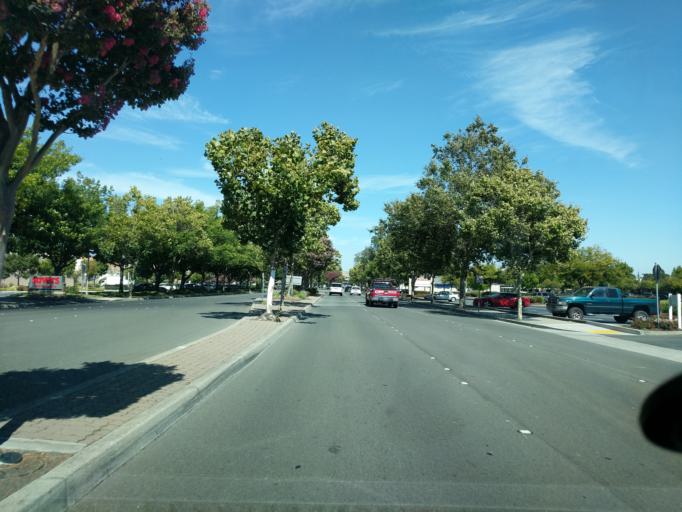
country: US
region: California
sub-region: Alameda County
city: Dublin
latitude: 37.7030
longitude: -121.9329
